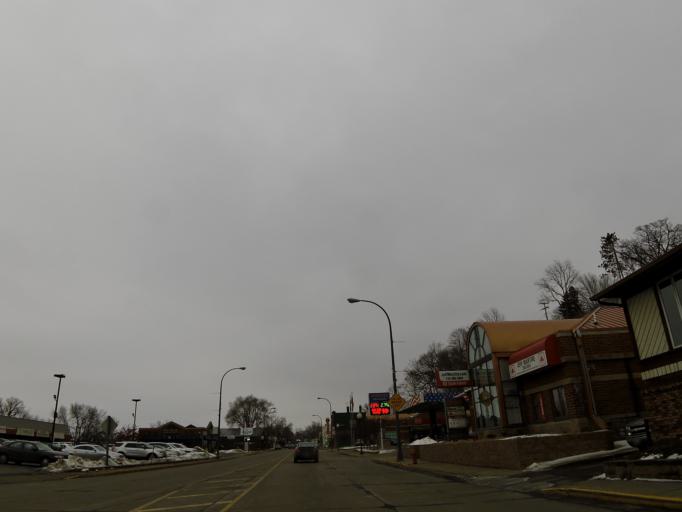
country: US
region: Wisconsin
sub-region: Saint Croix County
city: Hudson
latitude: 44.9718
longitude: -92.7566
